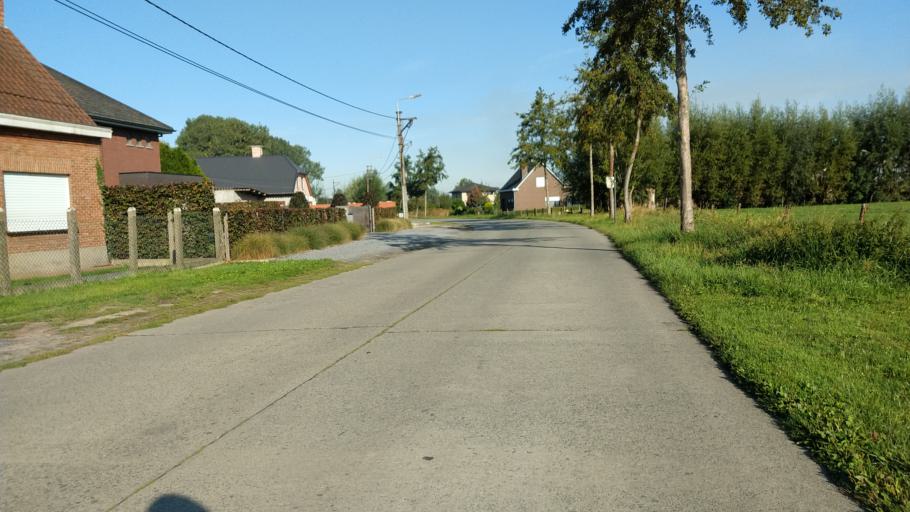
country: BE
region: Flanders
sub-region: Provincie Oost-Vlaanderen
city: Lochristi
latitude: 51.1375
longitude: 3.8294
